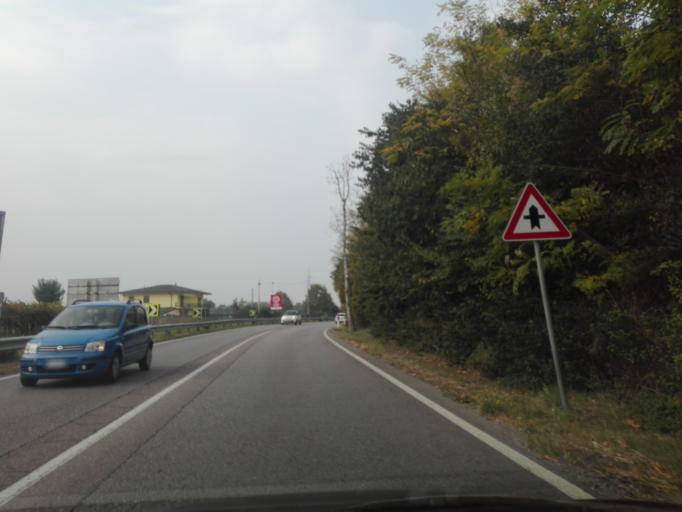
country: IT
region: Veneto
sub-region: Provincia di Verona
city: San Giorgio in Salici
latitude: 45.4399
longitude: 10.8021
